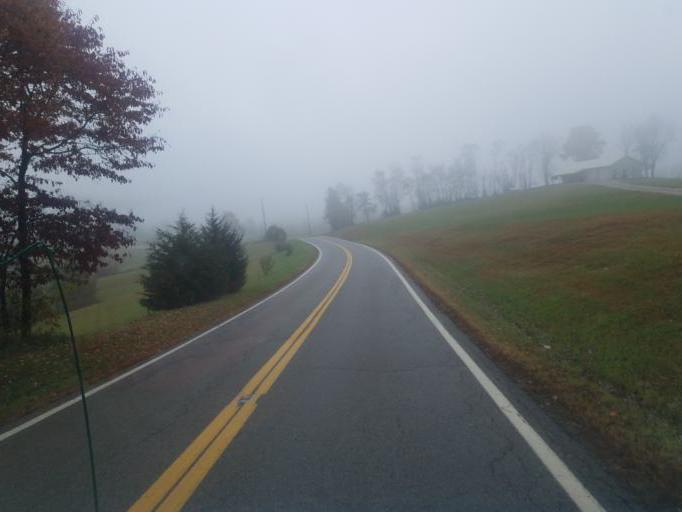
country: US
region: Ohio
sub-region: Morgan County
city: McConnelsville
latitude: 39.5257
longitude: -81.7932
